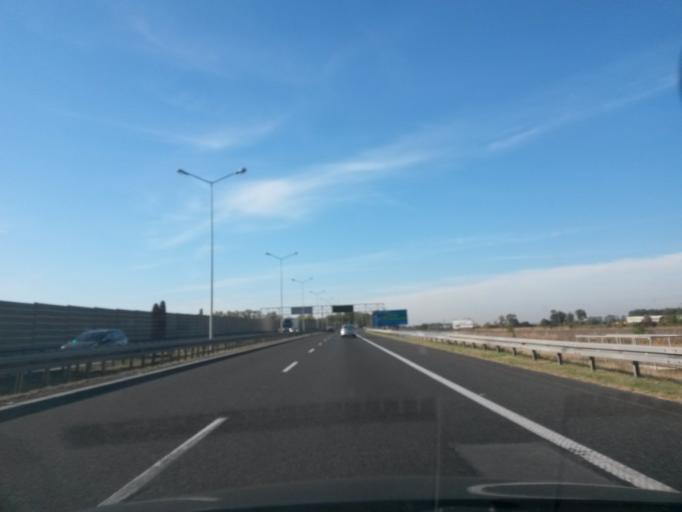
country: PL
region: Lower Silesian Voivodeship
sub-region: Powiat wroclawski
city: Zorawina
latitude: 50.9608
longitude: 17.0716
